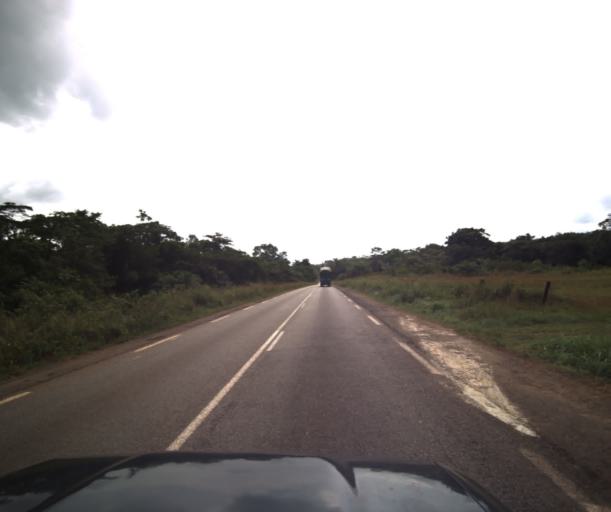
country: CM
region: Littoral
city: Edea
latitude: 3.8156
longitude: 10.3507
